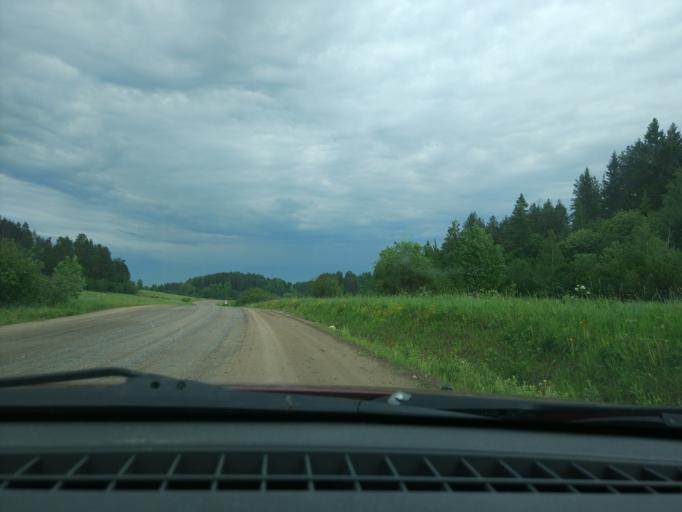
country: RU
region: Leningrad
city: Kuznechnoye
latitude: 61.2767
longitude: 29.8479
